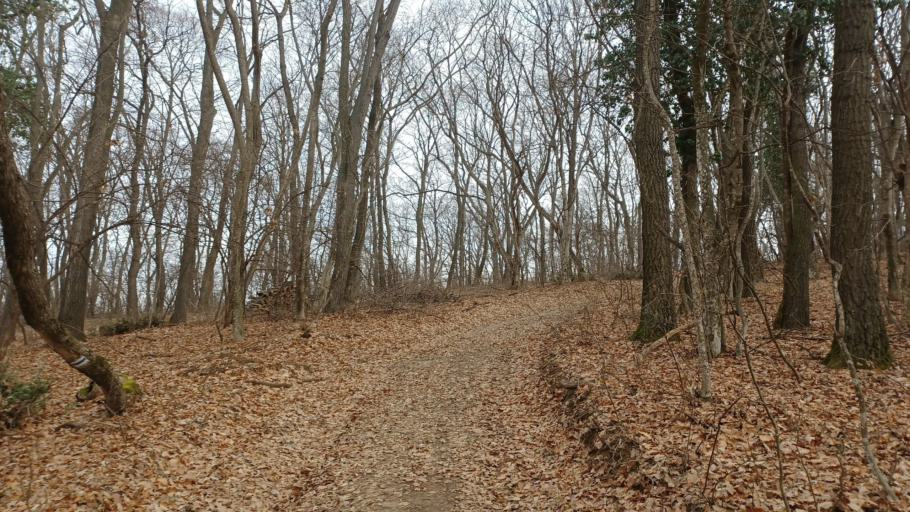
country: HU
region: Tolna
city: Szentgalpuszta
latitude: 46.3354
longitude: 18.6278
